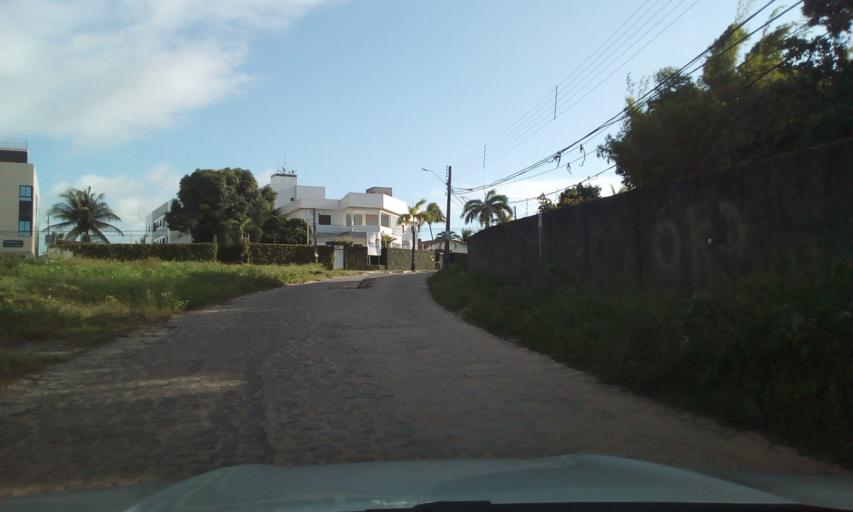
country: BR
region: Paraiba
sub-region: Joao Pessoa
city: Joao Pessoa
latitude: -7.1626
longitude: -34.8520
